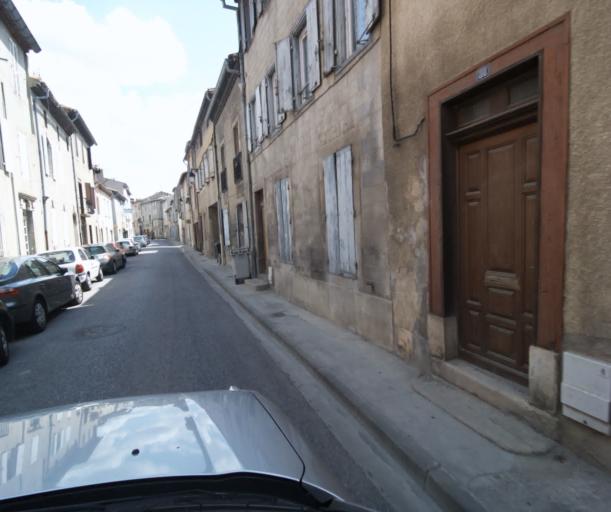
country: FR
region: Languedoc-Roussillon
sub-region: Departement de l'Aude
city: Limoux
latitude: 43.0553
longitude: 2.2203
